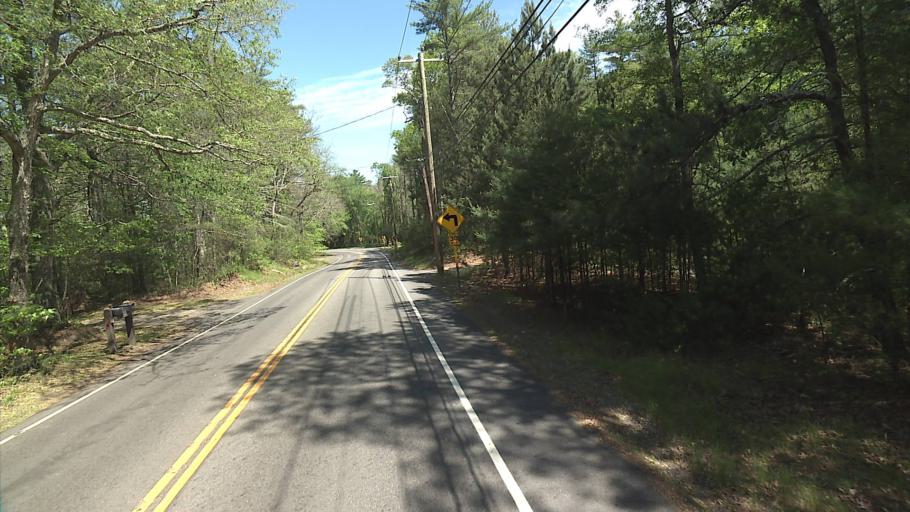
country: US
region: Connecticut
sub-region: New London County
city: Preston City
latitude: 41.5680
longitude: -71.8579
